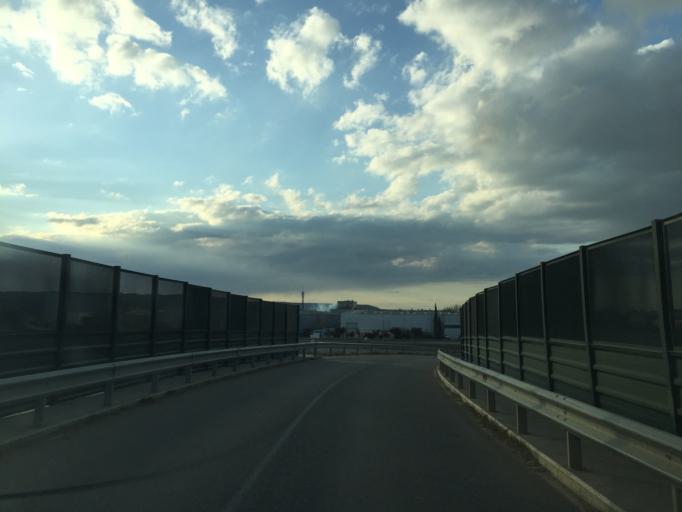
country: ES
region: Castille and Leon
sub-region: Provincia de Palencia
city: Venta de Banos
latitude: 41.9284
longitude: -4.4830
